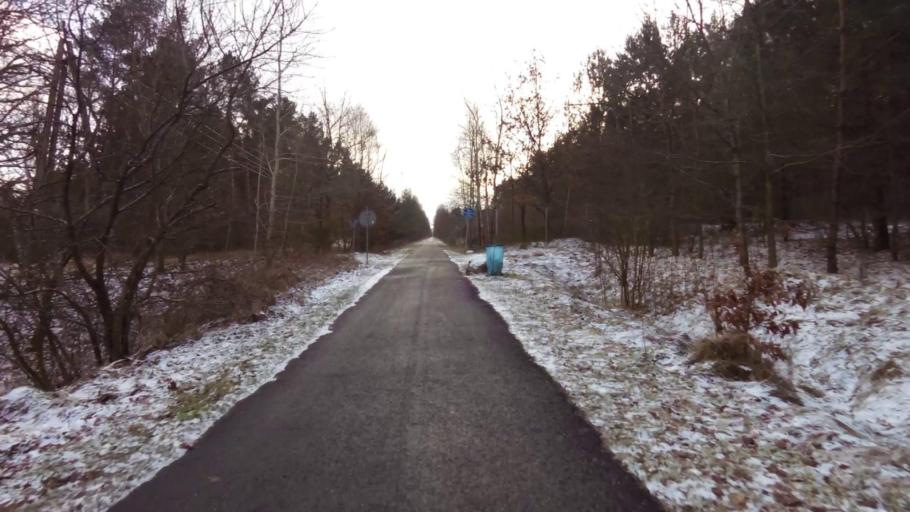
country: PL
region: West Pomeranian Voivodeship
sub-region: Powiat drawski
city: Zlocieniec
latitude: 53.5777
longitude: 16.0394
